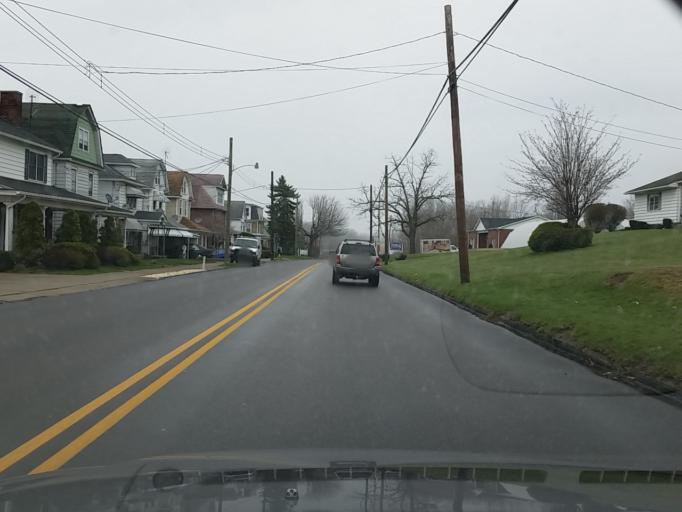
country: US
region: Pennsylvania
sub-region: Luzerne County
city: Nanticoke
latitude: 41.2074
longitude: -75.9891
